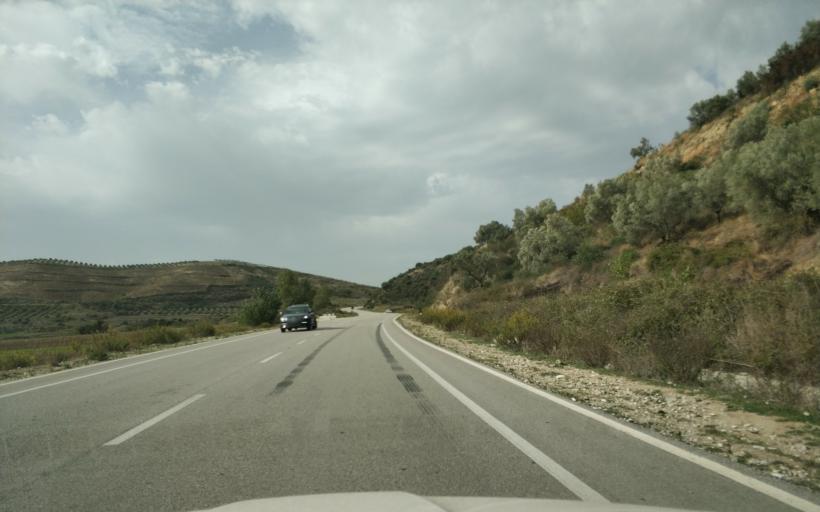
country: AL
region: Gjirokaster
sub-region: Rrethi i Tepelenes
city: Krahes
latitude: 40.3913
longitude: 19.8766
